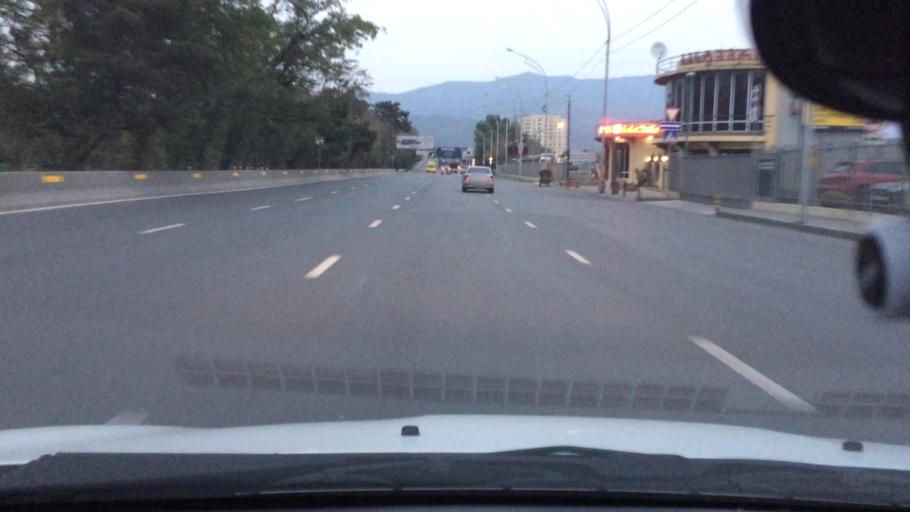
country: GE
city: Zahesi
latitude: 41.7899
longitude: 44.7703
